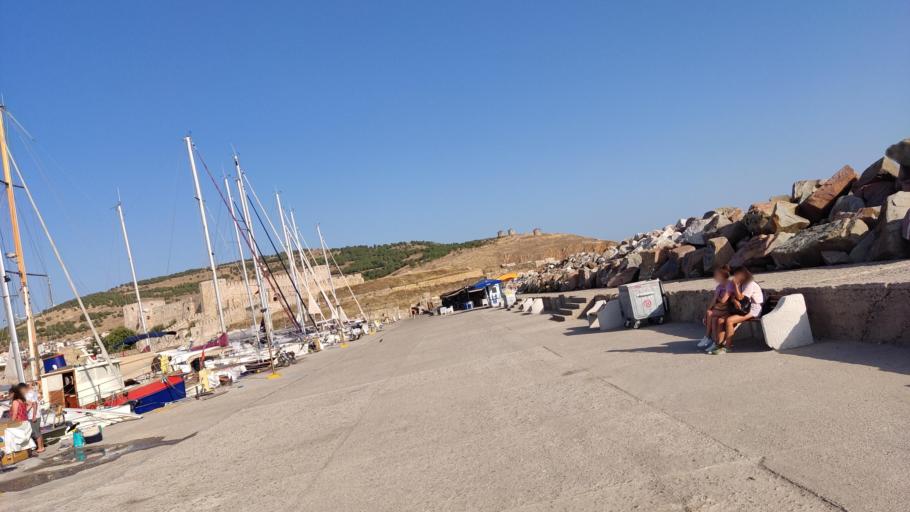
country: TR
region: Canakkale
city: Bozcaada
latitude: 39.8359
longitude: 26.0757
